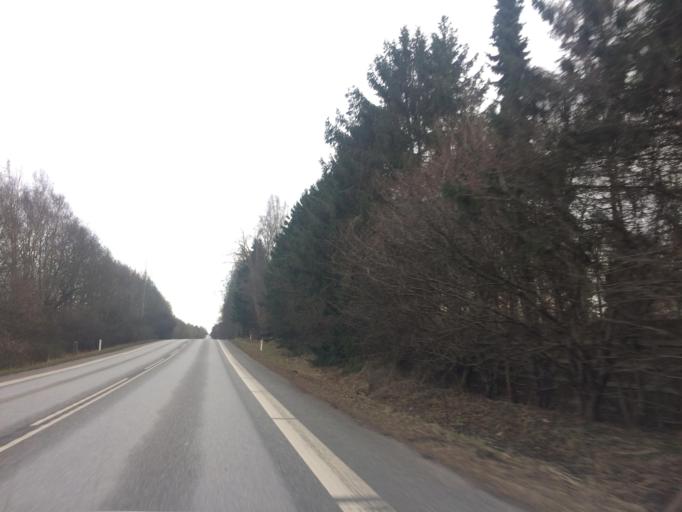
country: DK
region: Capital Region
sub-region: Fredensborg Kommune
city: Fredensborg
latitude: 55.9579
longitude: 12.4132
